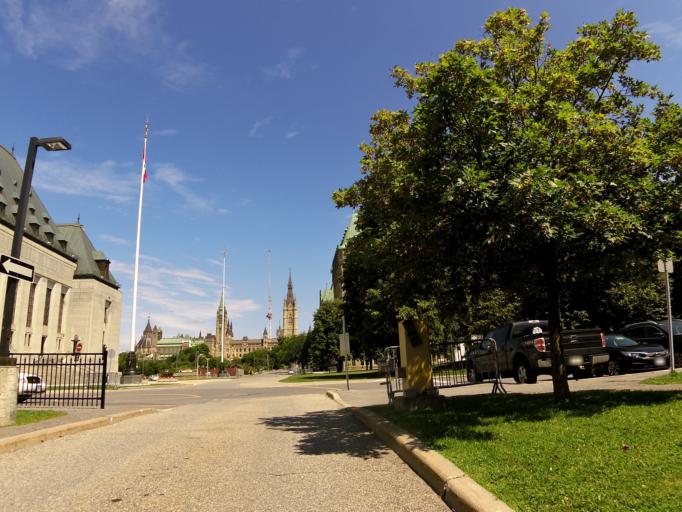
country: CA
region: Ontario
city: Ottawa
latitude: 45.4211
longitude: -75.7058
